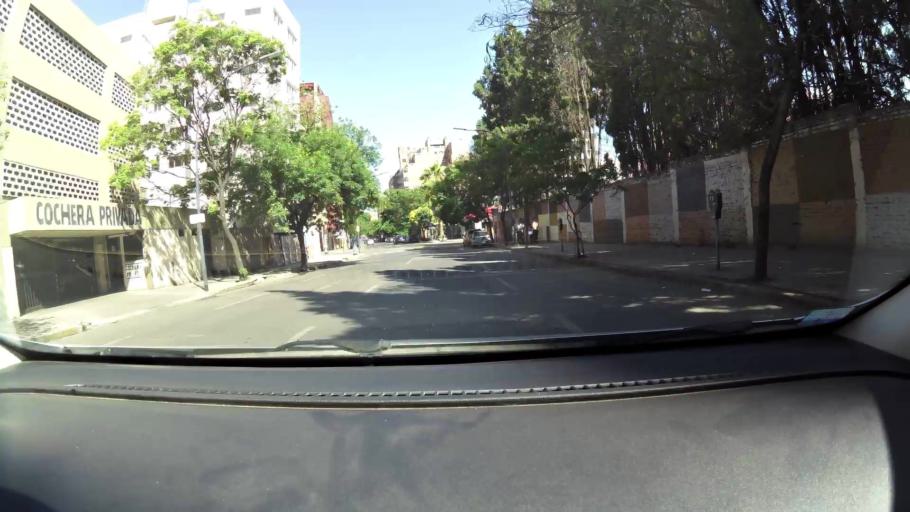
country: AR
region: Cordoba
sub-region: Departamento de Capital
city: Cordoba
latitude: -31.4165
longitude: -64.1957
